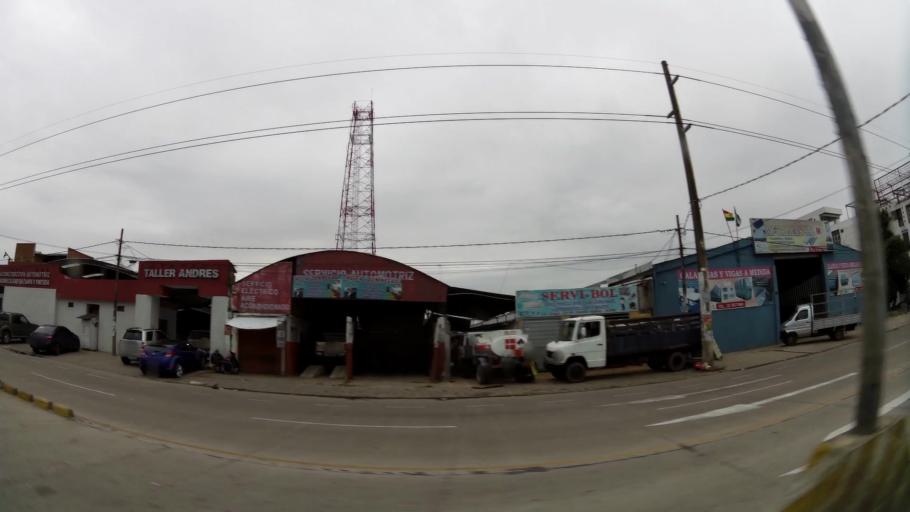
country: BO
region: Santa Cruz
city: Santa Cruz de la Sierra
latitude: -17.7883
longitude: -63.2049
